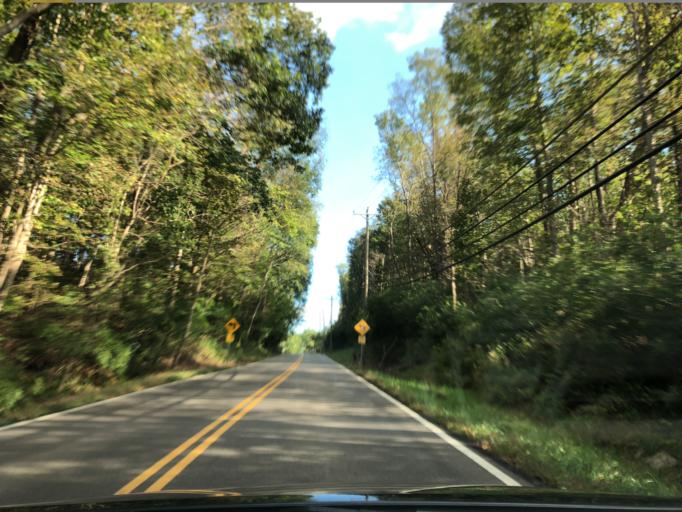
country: US
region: Ohio
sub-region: Hamilton County
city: Loveland
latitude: 39.2577
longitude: -84.2663
